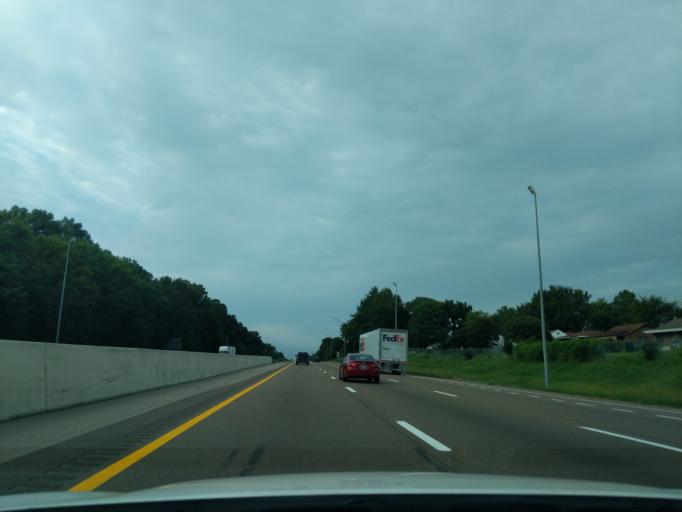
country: US
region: Tennessee
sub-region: Shelby County
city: New South Memphis
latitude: 35.0914
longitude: -90.0766
